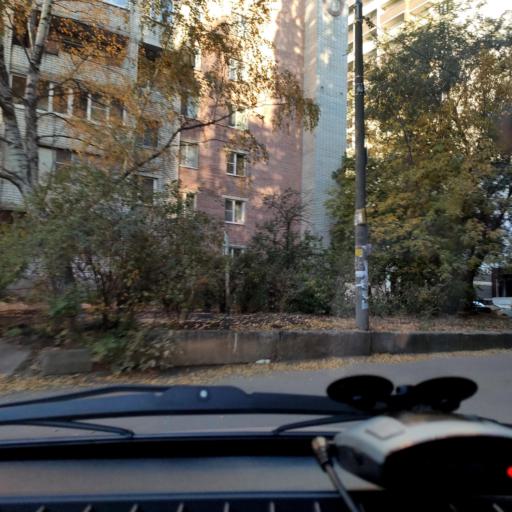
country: RU
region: Voronezj
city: Voronezh
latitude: 51.6852
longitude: 39.1948
